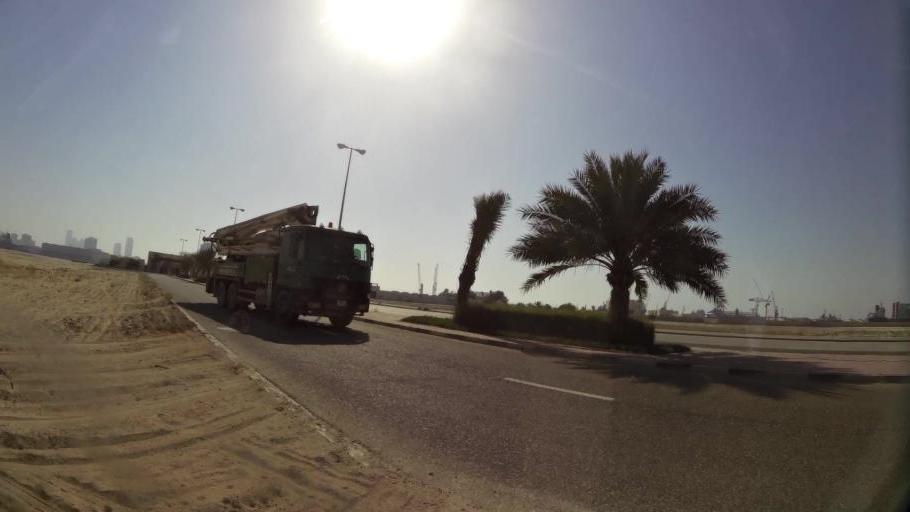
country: AE
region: Ajman
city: Ajman
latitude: 25.4199
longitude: 55.4639
